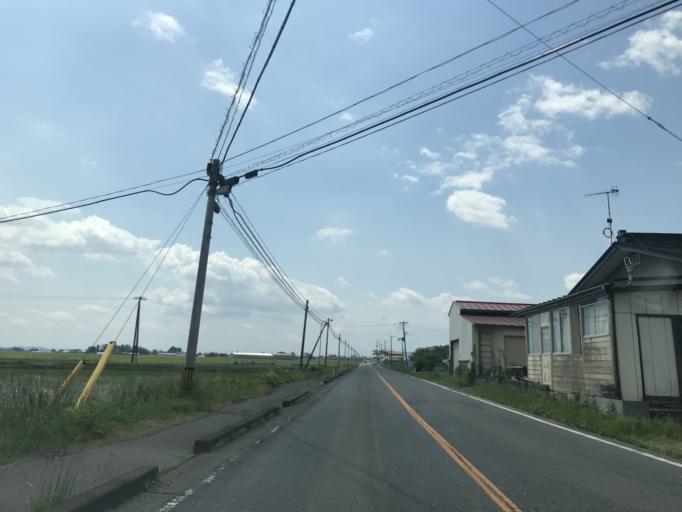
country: JP
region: Miyagi
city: Kogota
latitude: 38.6170
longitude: 141.0192
